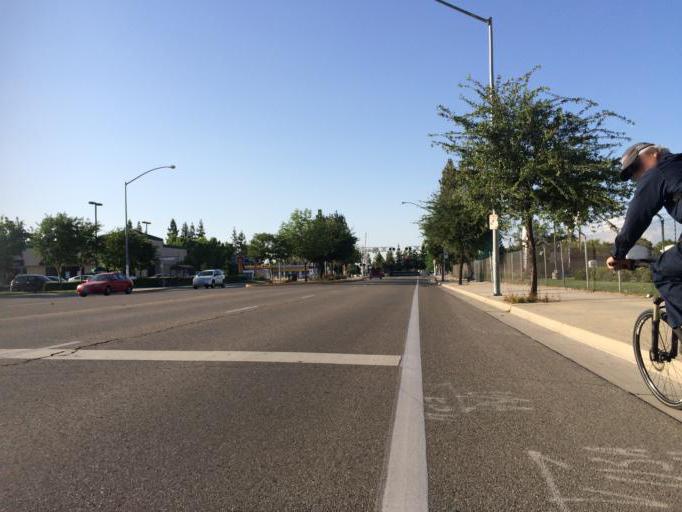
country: US
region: California
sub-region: Fresno County
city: Sunnyside
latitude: 36.7636
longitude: -119.7182
